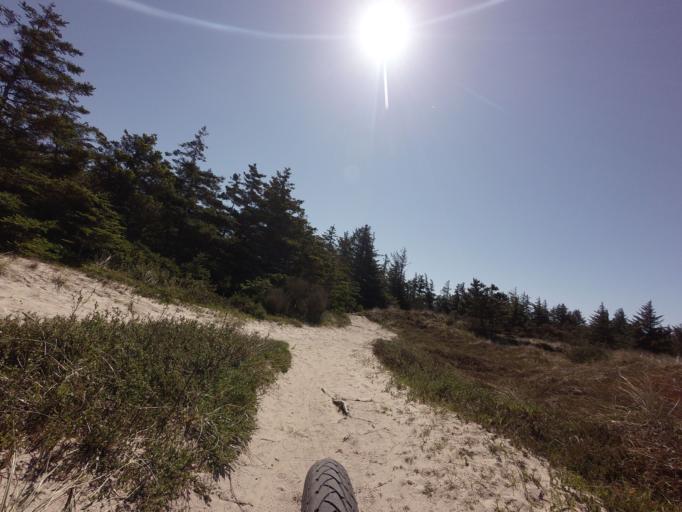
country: DK
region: North Denmark
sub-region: Jammerbugt Kommune
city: Pandrup
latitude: 57.2939
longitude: 9.6456
